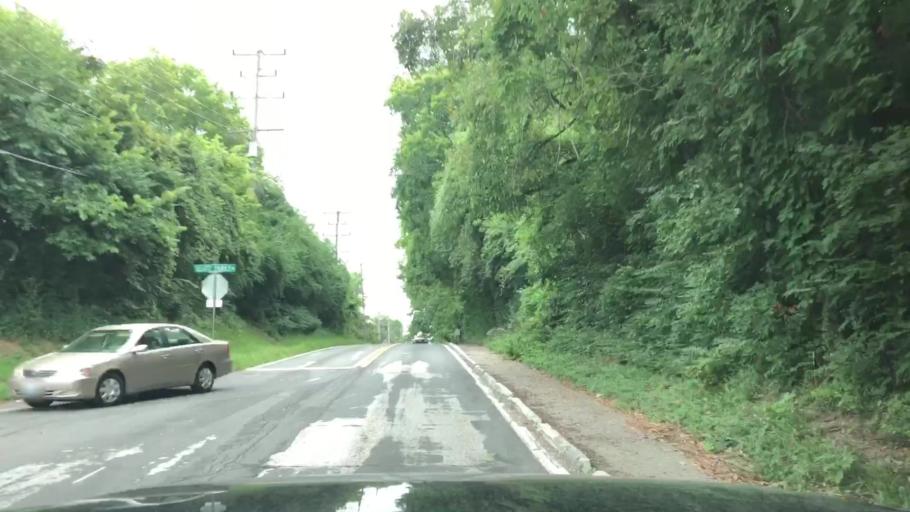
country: US
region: Missouri
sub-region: Saint Louis County
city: Hazelwood
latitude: 38.8142
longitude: -90.3676
